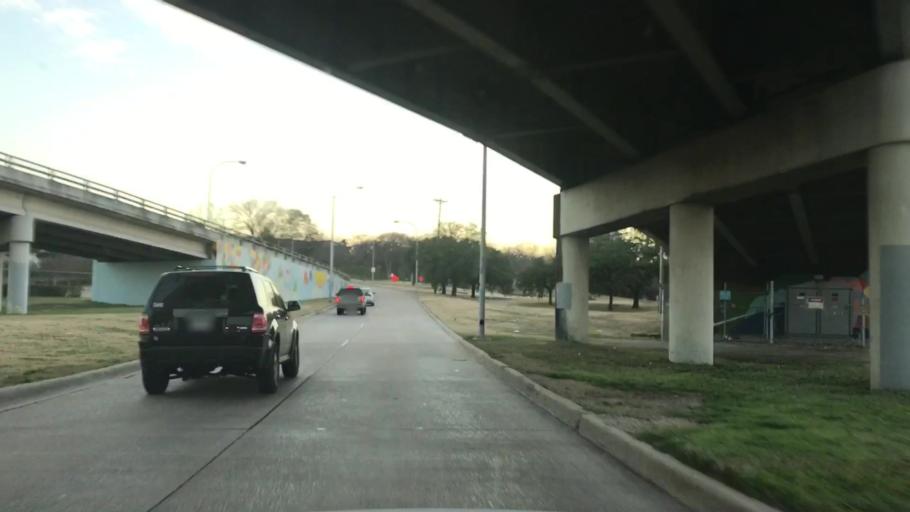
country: US
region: Texas
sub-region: Dallas County
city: Dallas
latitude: 32.7624
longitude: -96.8148
